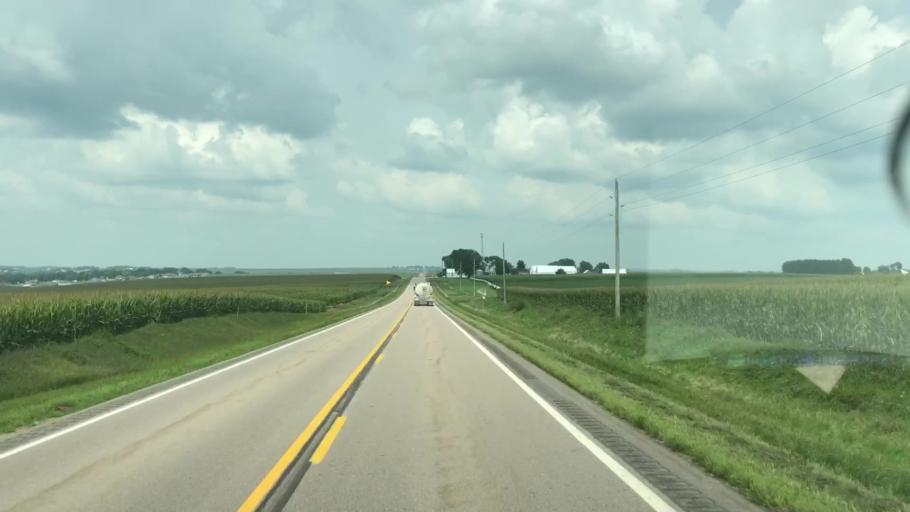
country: US
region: Iowa
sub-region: Plymouth County
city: Remsen
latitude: 42.7993
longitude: -95.9577
